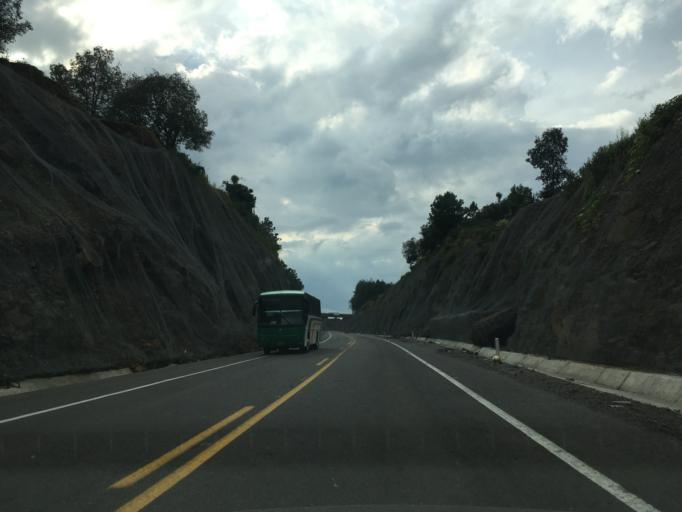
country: MX
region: Michoacan
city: Angahuan
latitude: 19.5081
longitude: -102.1552
